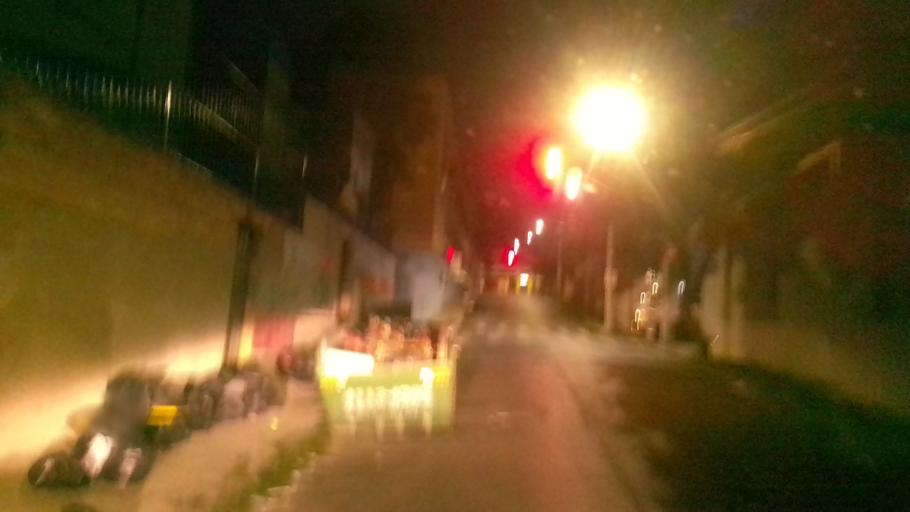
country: BR
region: Minas Gerais
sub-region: Belo Horizonte
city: Belo Horizonte
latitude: -19.9105
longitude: -43.9603
